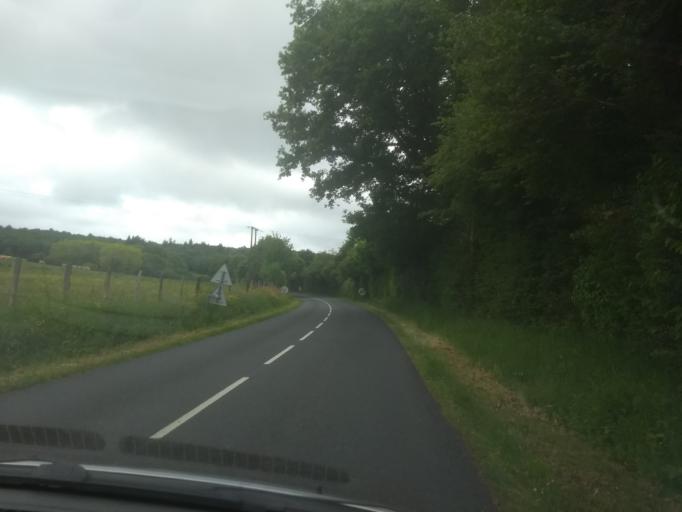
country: FR
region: Lower Normandy
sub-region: Departement de l'Orne
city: Bretoncelles
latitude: 48.4721
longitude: 0.8402
